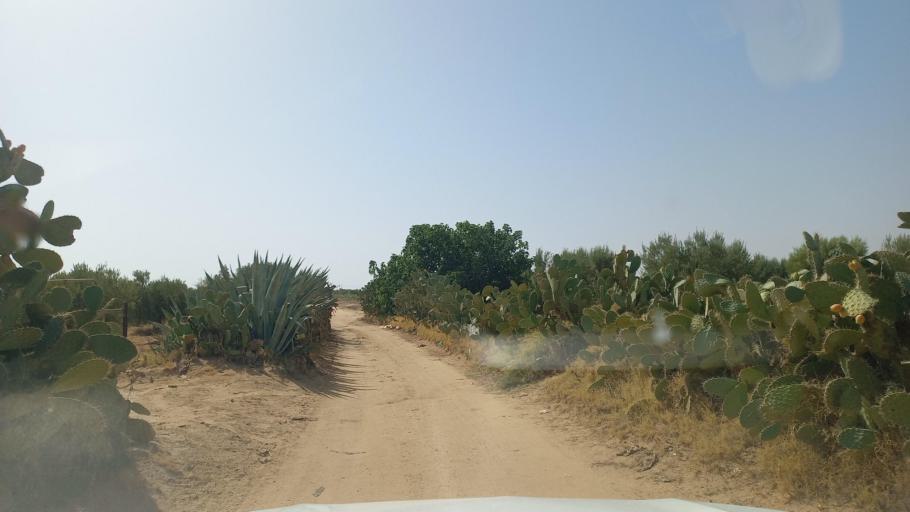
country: TN
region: Al Qasrayn
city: Kasserine
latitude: 35.2416
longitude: 9.0490
